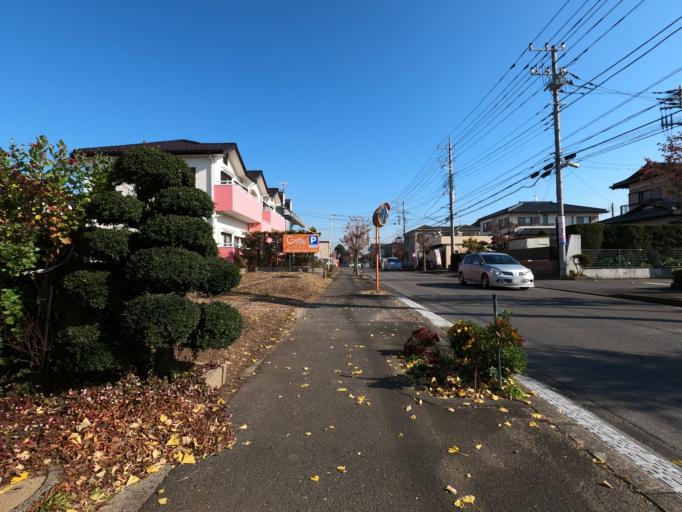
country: JP
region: Ibaraki
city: Moriya
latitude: 35.9365
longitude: 139.9920
